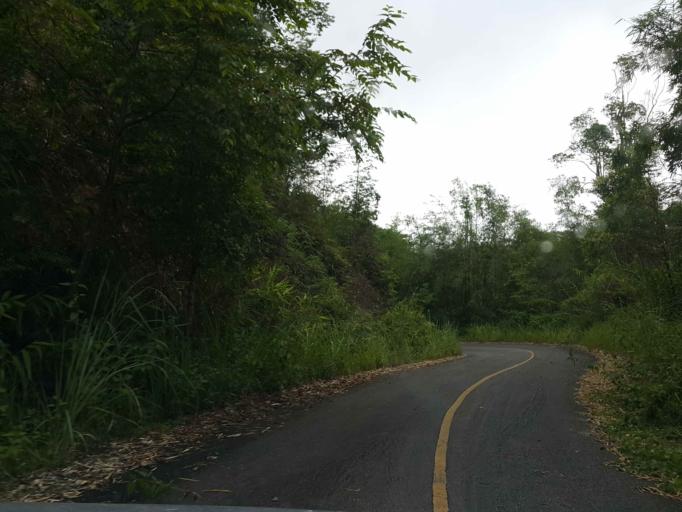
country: TH
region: Tak
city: Tak
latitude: 16.7876
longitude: 98.9232
